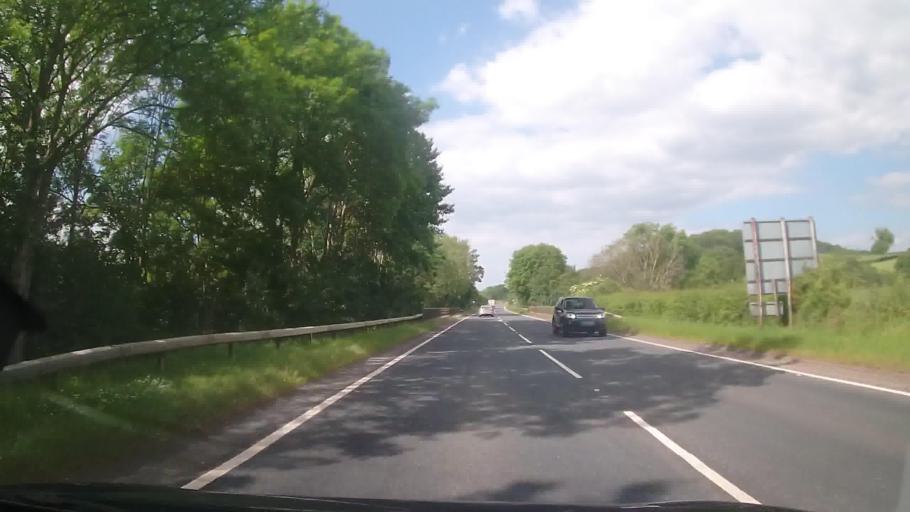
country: GB
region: England
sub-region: Shropshire
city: Ludlow
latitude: 52.3402
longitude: -2.7117
